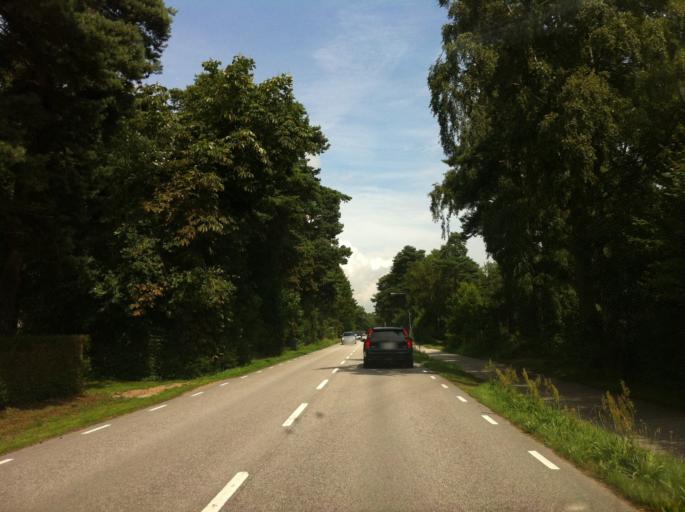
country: SE
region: Skane
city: Smygehamn
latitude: 55.3646
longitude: 13.4322
